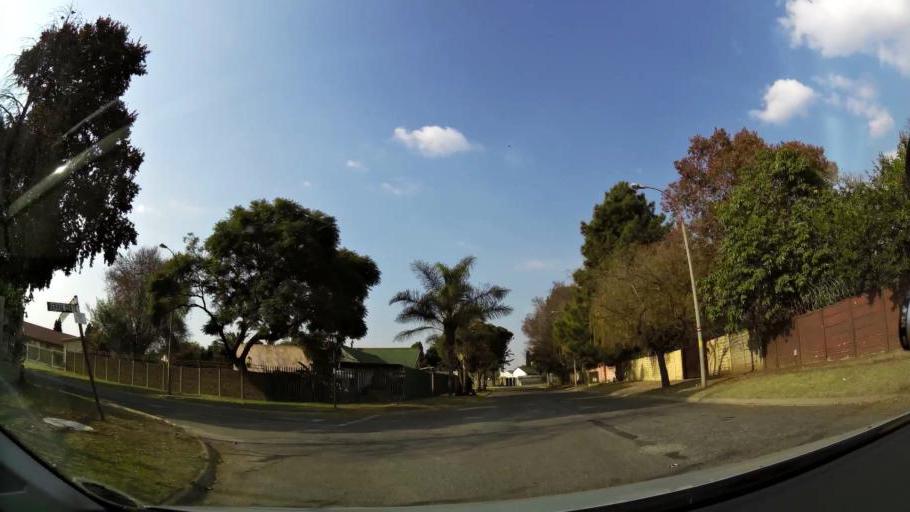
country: ZA
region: Gauteng
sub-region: City of Johannesburg Metropolitan Municipality
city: Modderfontein
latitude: -26.1035
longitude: 28.1924
